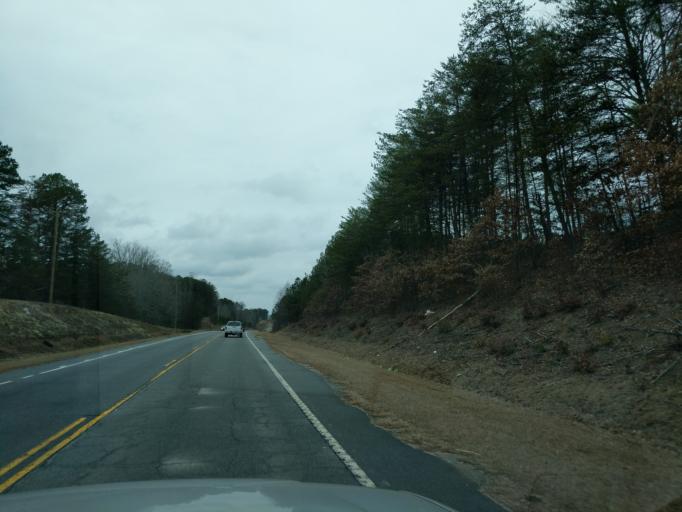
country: US
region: South Carolina
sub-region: Oconee County
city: Walhalla
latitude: 34.9116
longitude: -82.9453
